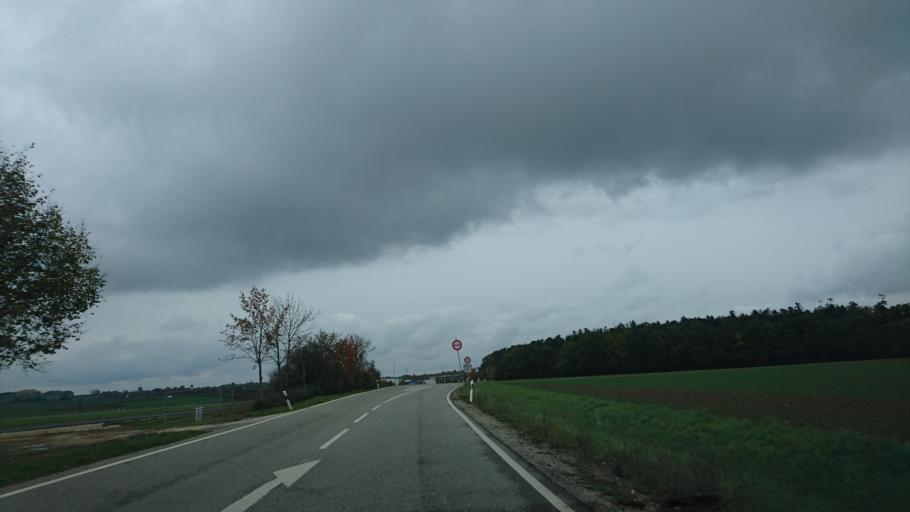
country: DE
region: Bavaria
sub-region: Regierungsbezirk Mittelfranken
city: Thalmassing
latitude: 49.1518
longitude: 11.2589
